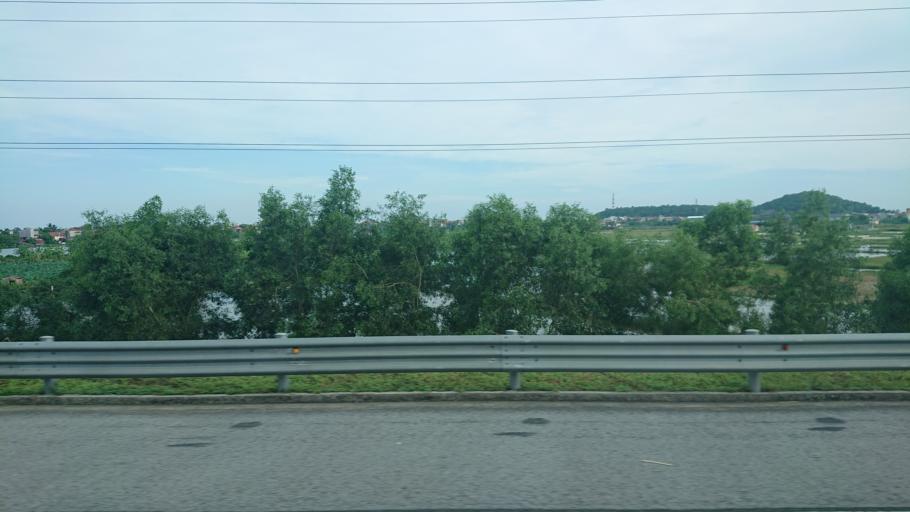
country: VN
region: Hai Phong
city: Nui Doi
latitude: 20.7654
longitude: 106.6730
